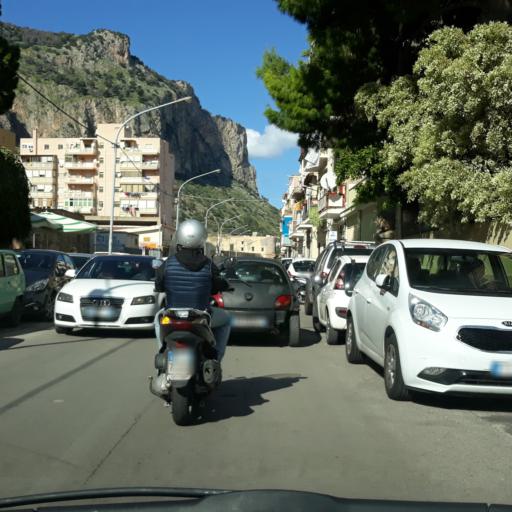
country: IT
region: Sicily
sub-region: Palermo
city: Palermo
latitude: 38.1636
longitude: 13.3699
